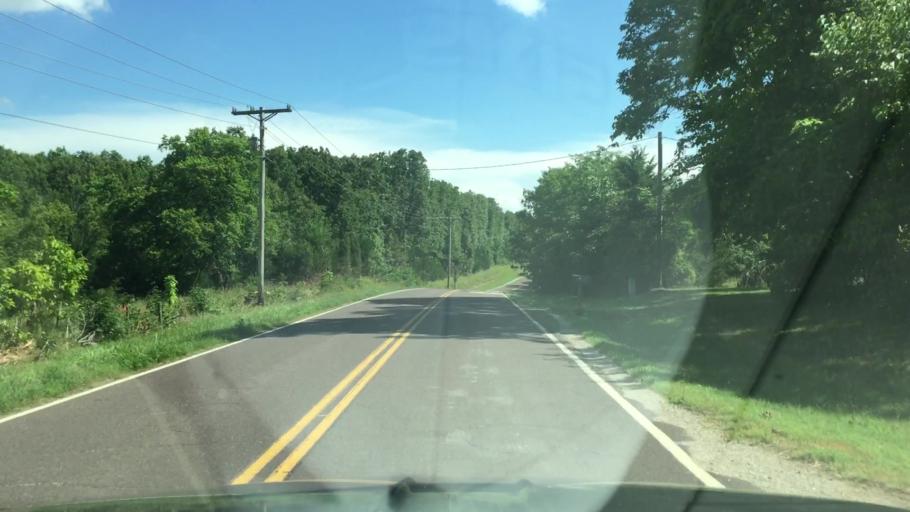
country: US
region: Missouri
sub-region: Miller County
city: Tuscumbia
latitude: 38.1168
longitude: -92.4717
